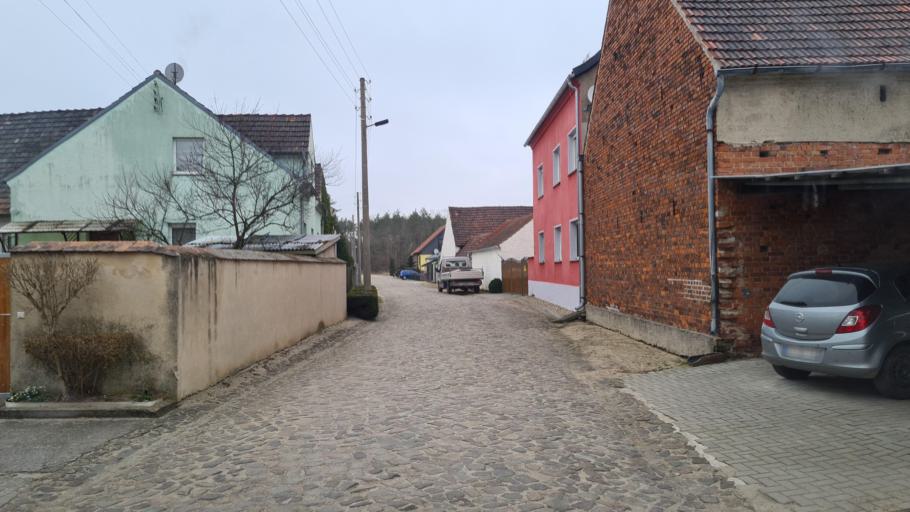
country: DE
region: Brandenburg
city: Herzberg
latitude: 51.6843
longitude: 13.1862
